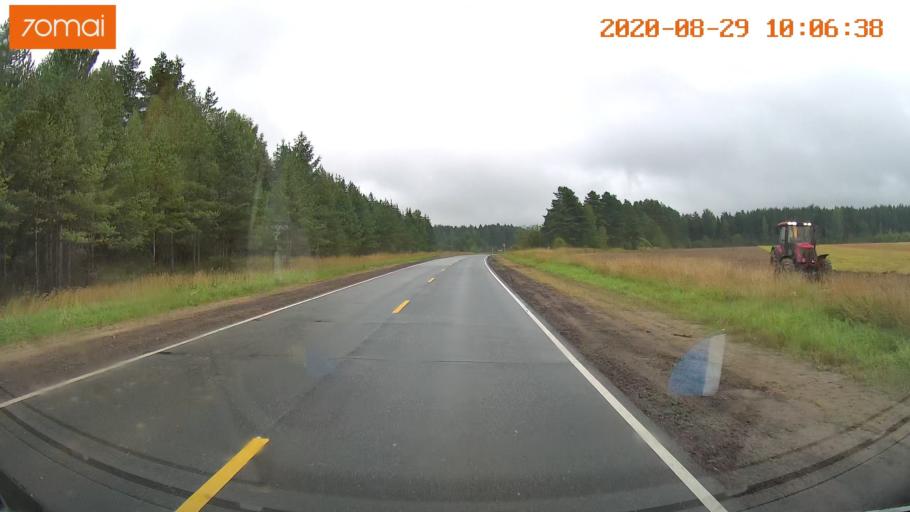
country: RU
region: Ivanovo
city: Kuznechikha
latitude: 57.3875
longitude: 42.5499
